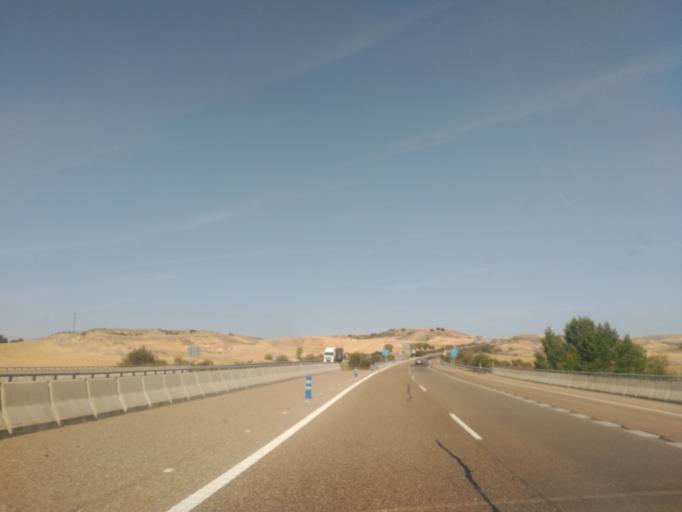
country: ES
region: Castille and Leon
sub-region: Provincia de Zamora
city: Castrillo de la Guarena
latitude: 41.2297
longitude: -5.3143
